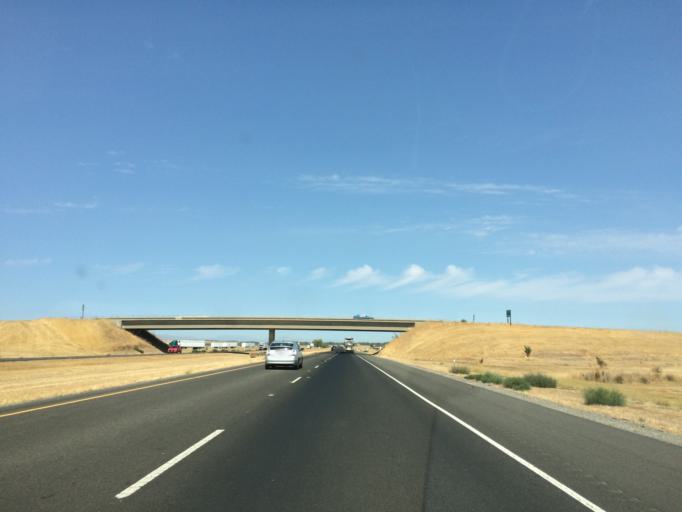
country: US
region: California
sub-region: Yolo County
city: Dunnigan
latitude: 38.8602
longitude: -121.9524
